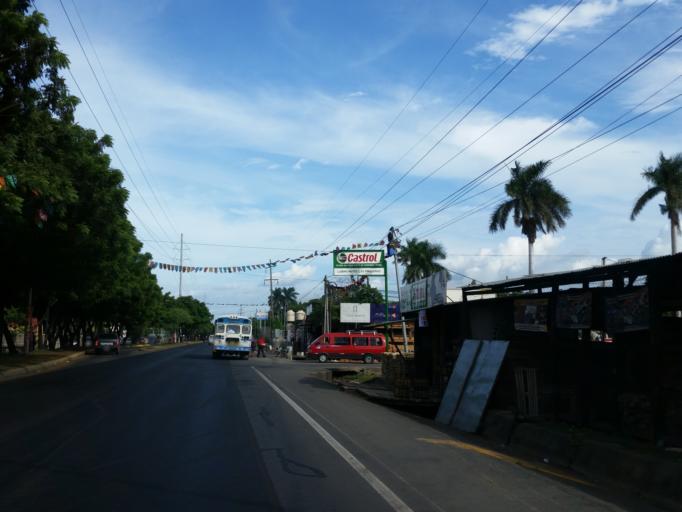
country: NI
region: Masaya
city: Ticuantepe
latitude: 12.0779
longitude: -86.2232
